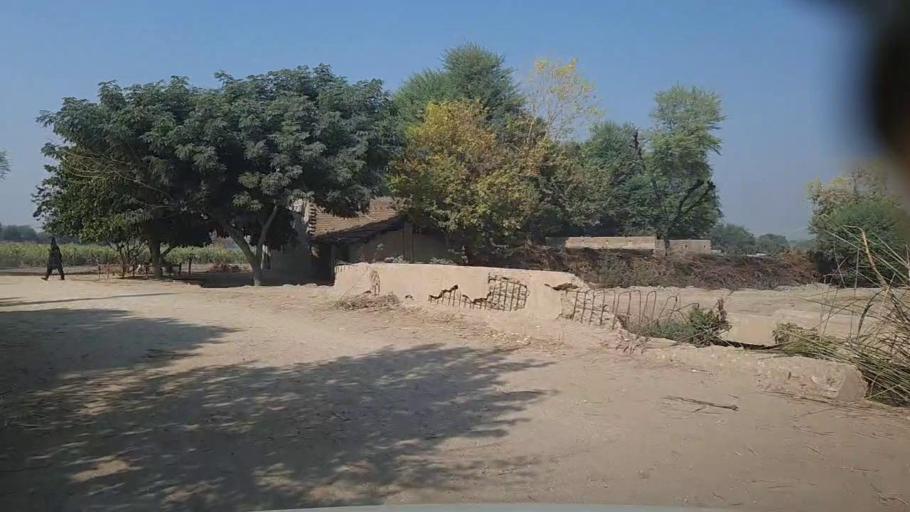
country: PK
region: Sindh
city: Kandiari
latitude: 26.9722
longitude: 68.4551
